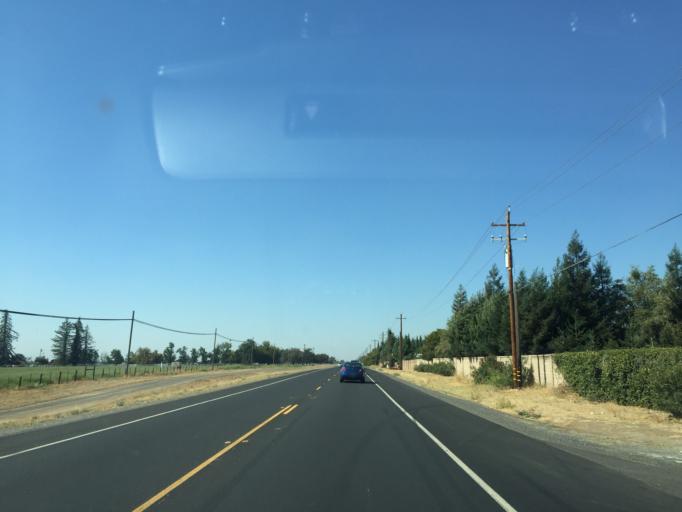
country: US
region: California
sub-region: Stanislaus County
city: East Oakdale
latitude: 37.7765
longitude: -120.7848
